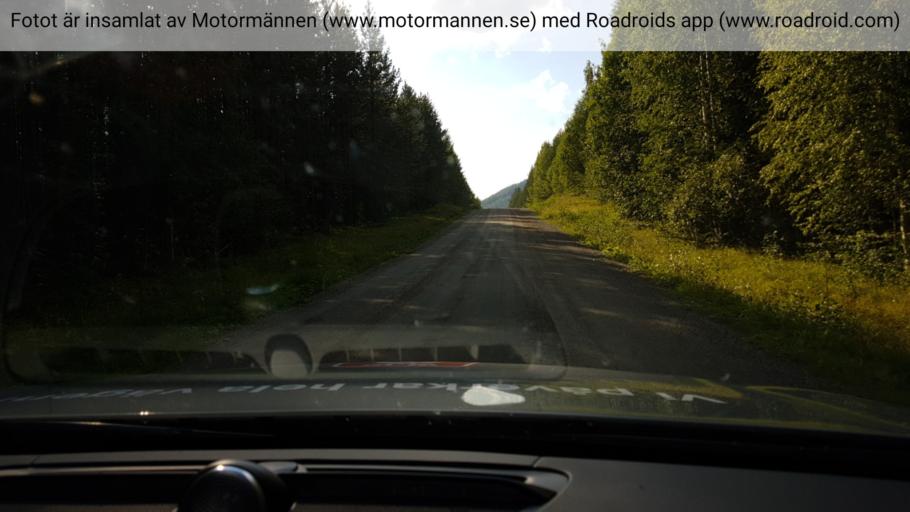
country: SE
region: Vaesternorrland
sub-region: Solleftea Kommun
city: As
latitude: 63.7768
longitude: 16.3482
